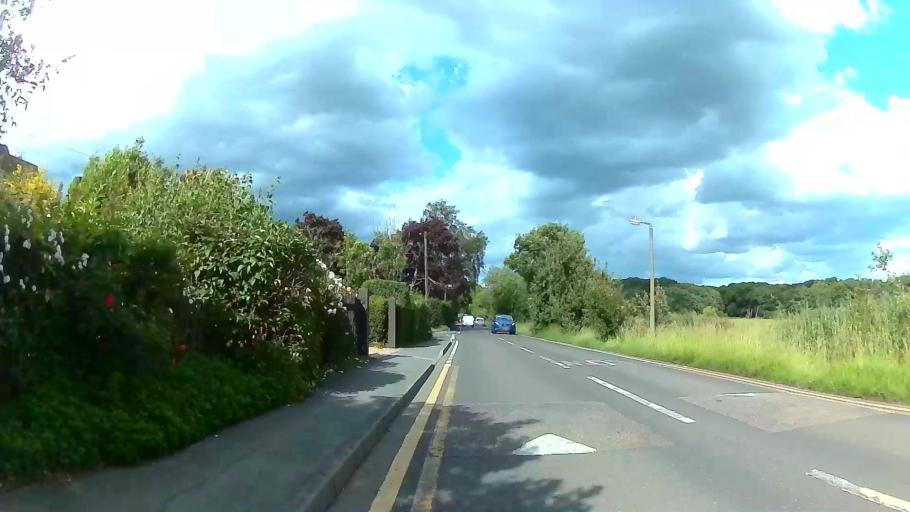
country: GB
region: England
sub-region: Greater London
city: Hainault
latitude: 51.6226
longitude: 0.1225
